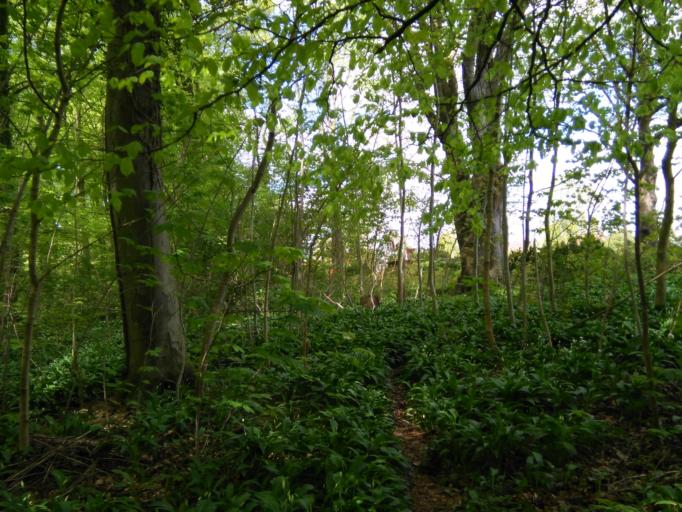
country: DK
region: Central Jutland
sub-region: Arhus Kommune
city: Arhus
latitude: 56.1814
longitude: 10.2275
